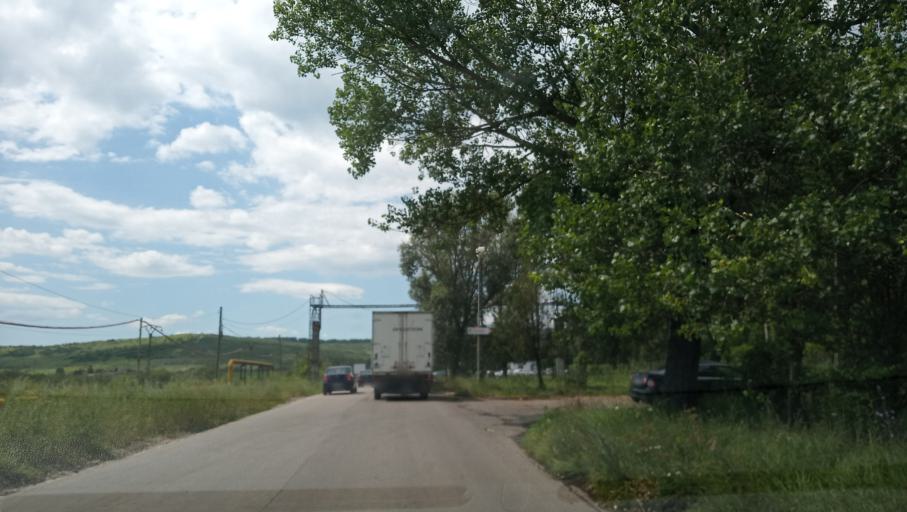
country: RO
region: Valcea
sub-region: Municipiul Ramnicu Valcea
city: Stolniceni
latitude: 45.0452
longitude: 24.2872
